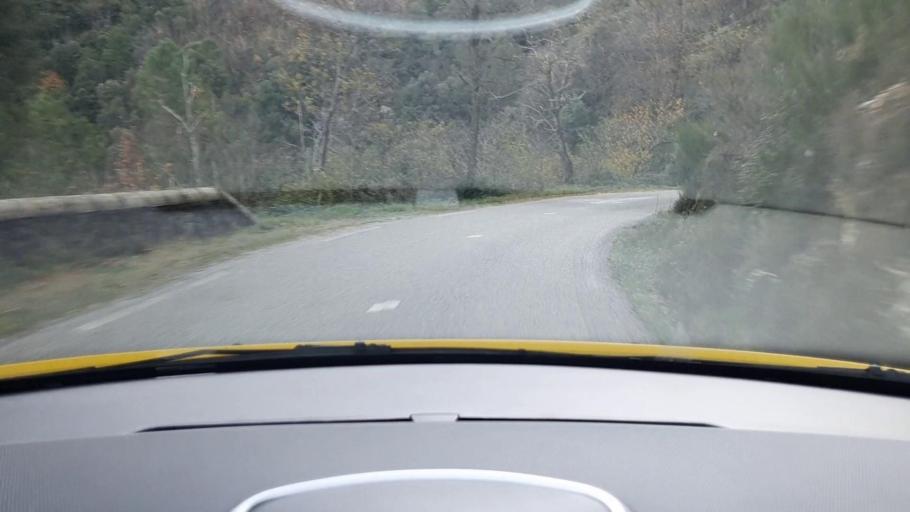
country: FR
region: Languedoc-Roussillon
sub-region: Departement du Gard
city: Branoux-les-Taillades
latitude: 44.2806
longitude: 3.9826
